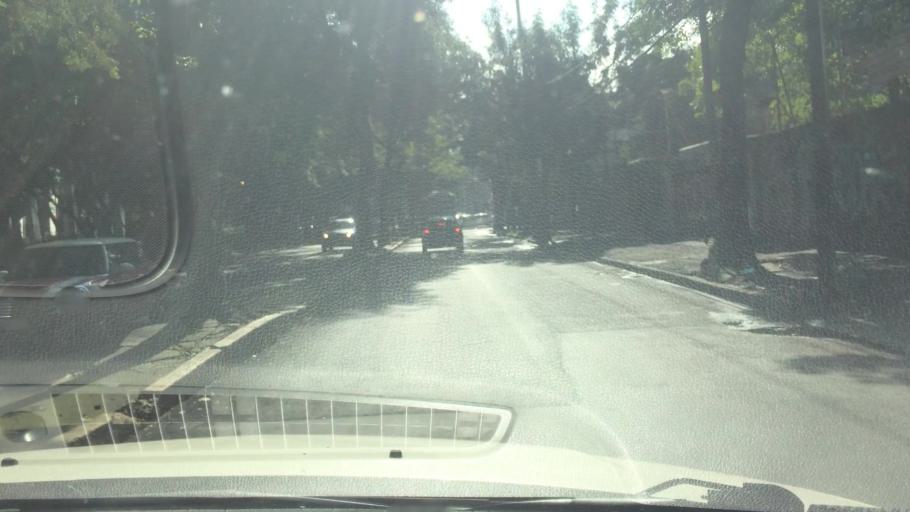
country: MX
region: Mexico City
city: Coyoacan
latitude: 19.3518
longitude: -99.1794
